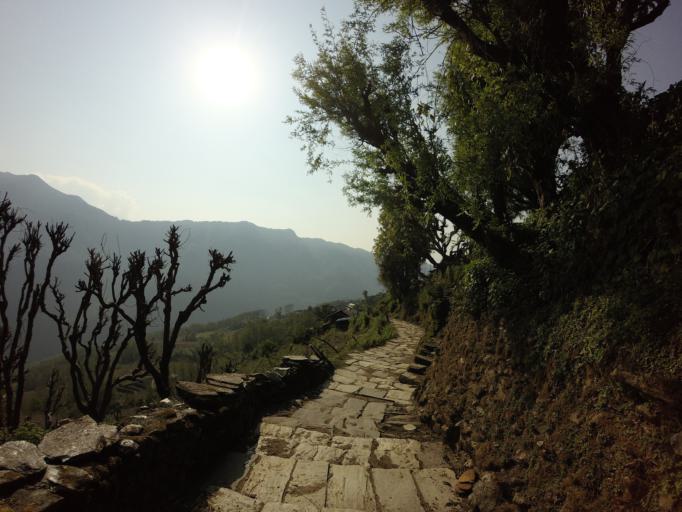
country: NP
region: Western Region
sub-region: Dhawalagiri Zone
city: Chitre
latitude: 28.3801
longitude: 83.8061
